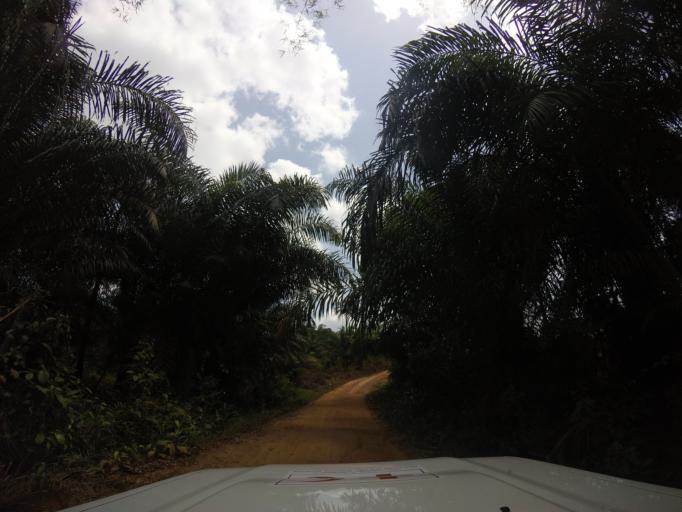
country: SL
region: Southern Province
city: Zimmi
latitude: 7.1989
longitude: -11.2169
